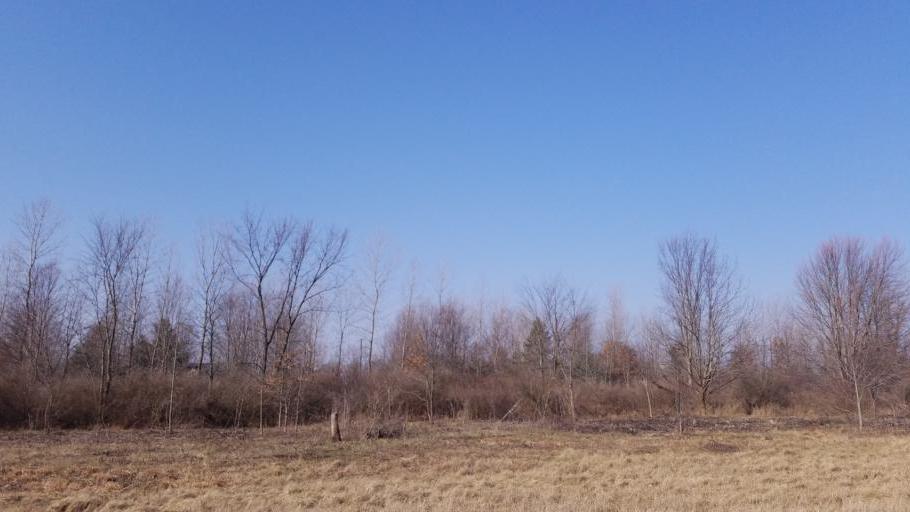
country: US
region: Ohio
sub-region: Crawford County
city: Galion
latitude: 40.7157
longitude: -82.7859
